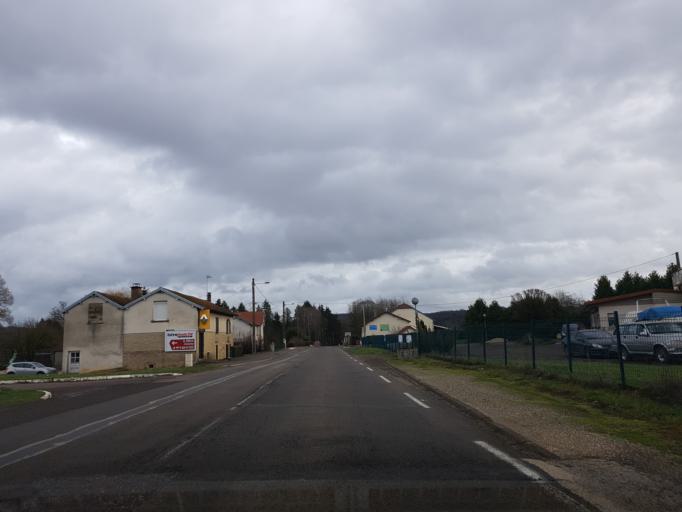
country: FR
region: Franche-Comte
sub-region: Departement de la Haute-Saone
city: Scey-sur-Saone-et-Saint-Albin
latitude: 47.7148
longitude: 5.8832
